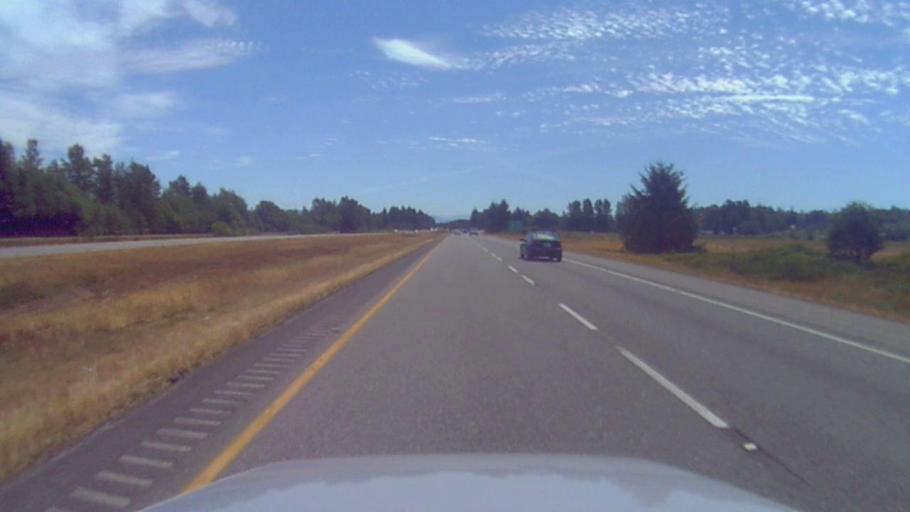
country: US
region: Washington
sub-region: Whatcom County
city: Ferndale
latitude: 48.8962
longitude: -122.6042
